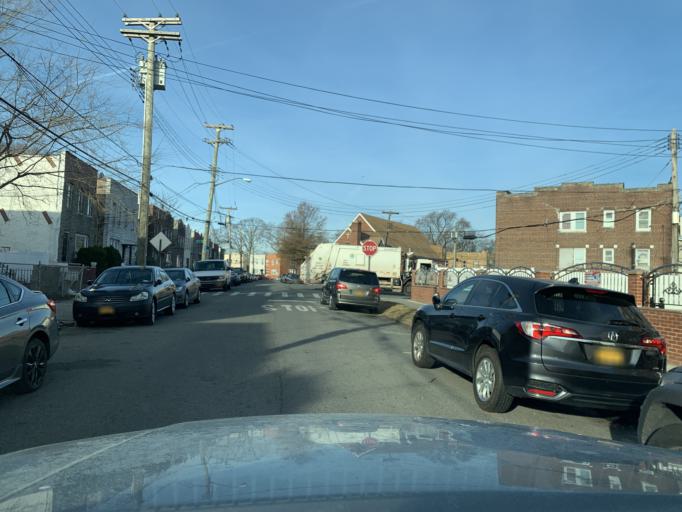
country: US
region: New York
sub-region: Queens County
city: Jamaica
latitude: 40.7021
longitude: -73.7800
